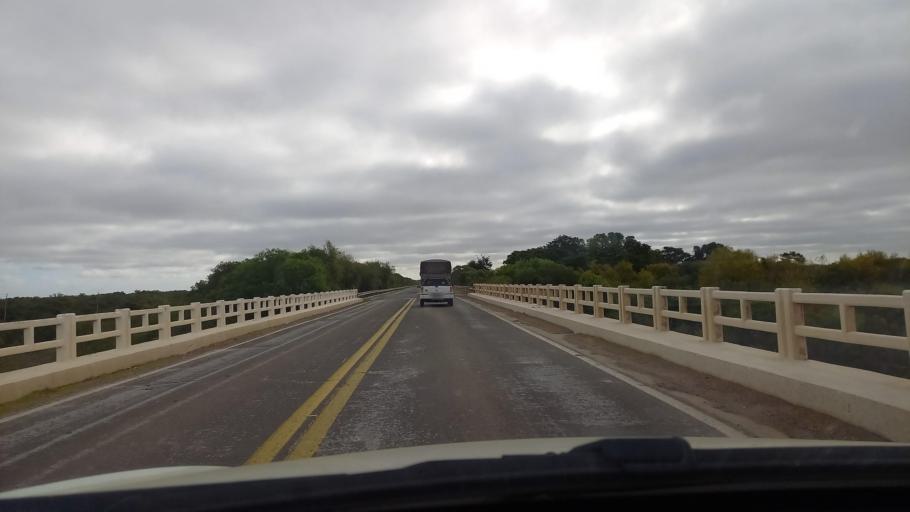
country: BR
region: Rio Grande do Sul
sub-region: Dom Pedrito
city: Dom Pedrito
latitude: -30.9485
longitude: -54.7113
